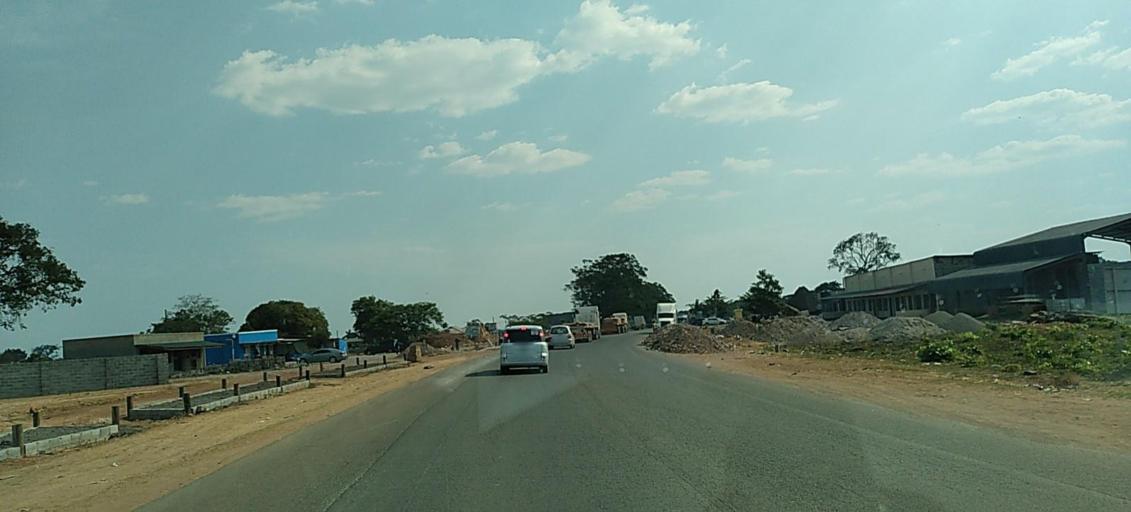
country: ZM
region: Copperbelt
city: Chililabombwe
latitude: -12.3681
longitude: 27.8531
